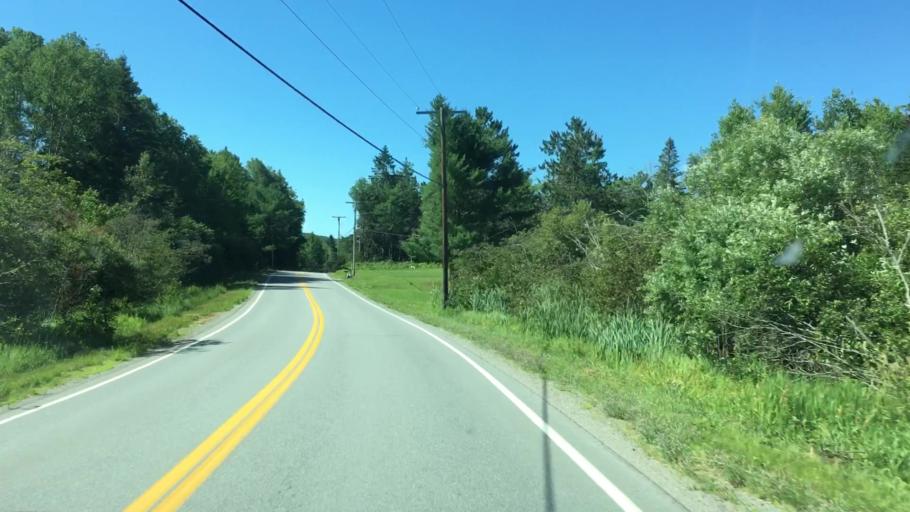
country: US
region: Maine
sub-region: Hancock County
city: Dedham
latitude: 44.7088
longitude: -68.6500
